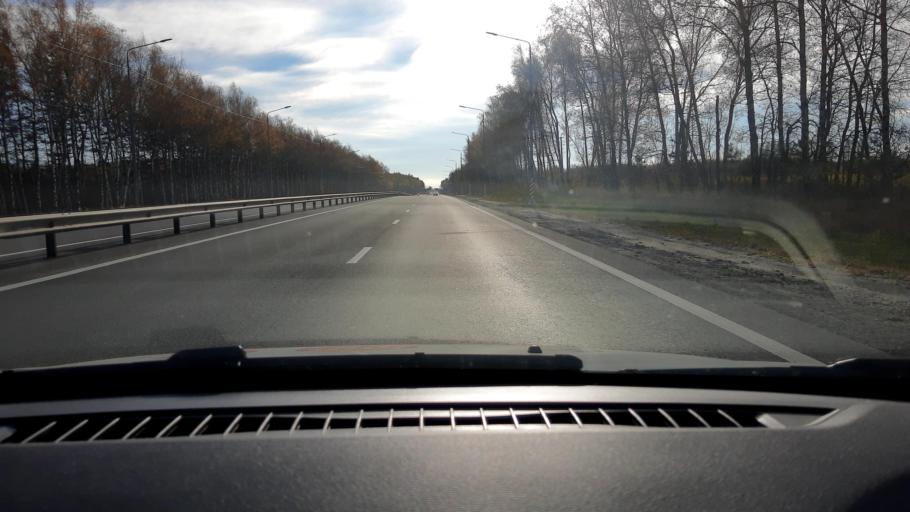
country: RU
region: Nizjnij Novgorod
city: Burevestnik
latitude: 56.0581
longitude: 43.9459
